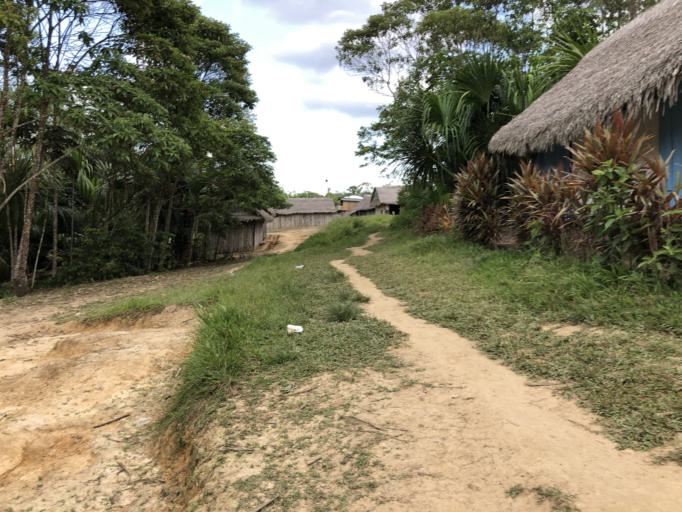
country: PE
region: Loreto
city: Puerto Galilea
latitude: -4.0580
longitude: -77.7604
